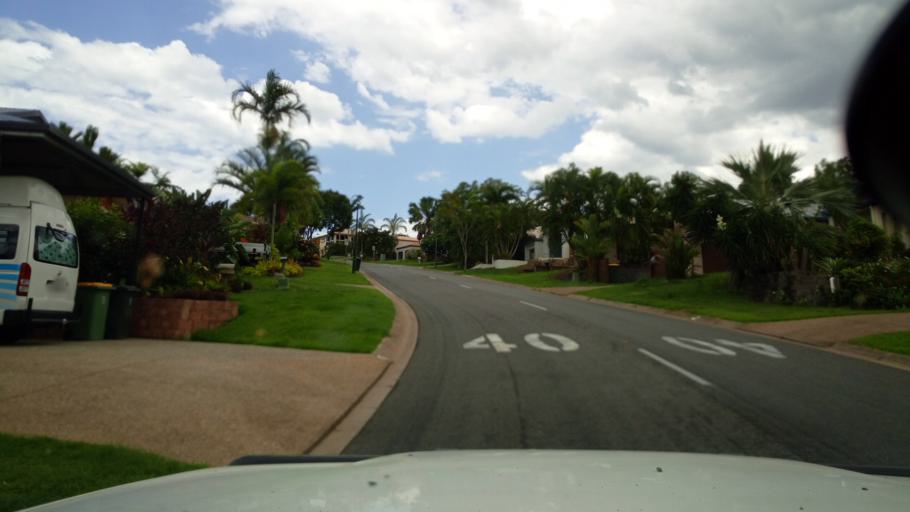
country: AU
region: Queensland
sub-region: Cairns
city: Redlynch
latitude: -16.9120
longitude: 145.7178
